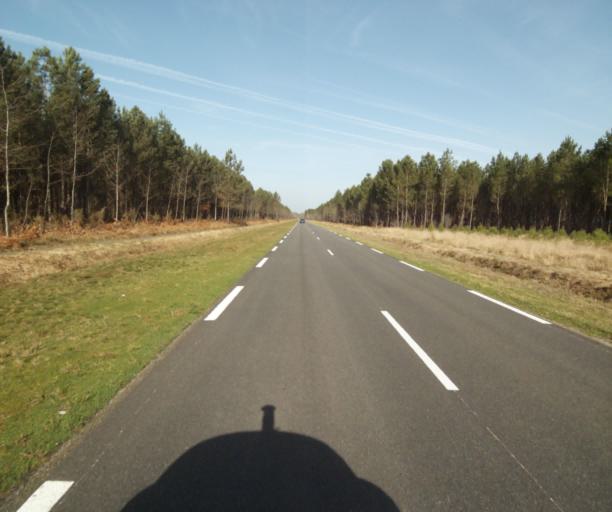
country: FR
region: Aquitaine
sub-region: Departement de la Gironde
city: Grignols
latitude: 44.1880
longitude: -0.1077
